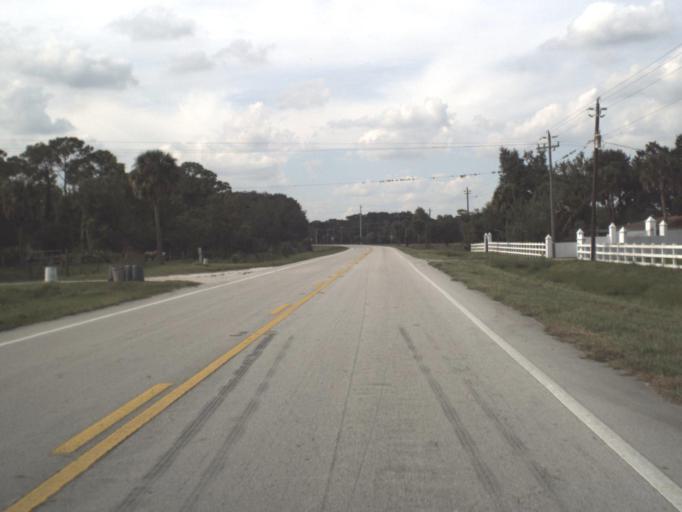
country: US
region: Florida
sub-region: Okeechobee County
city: Taylor Creek
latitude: 27.2319
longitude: -80.7749
